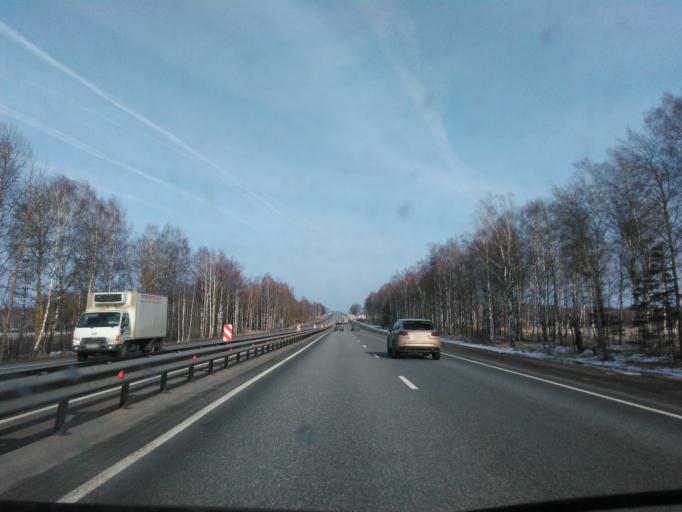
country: RU
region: Smolensk
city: Verkhnedneprovskiy
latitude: 55.1749
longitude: 33.4414
